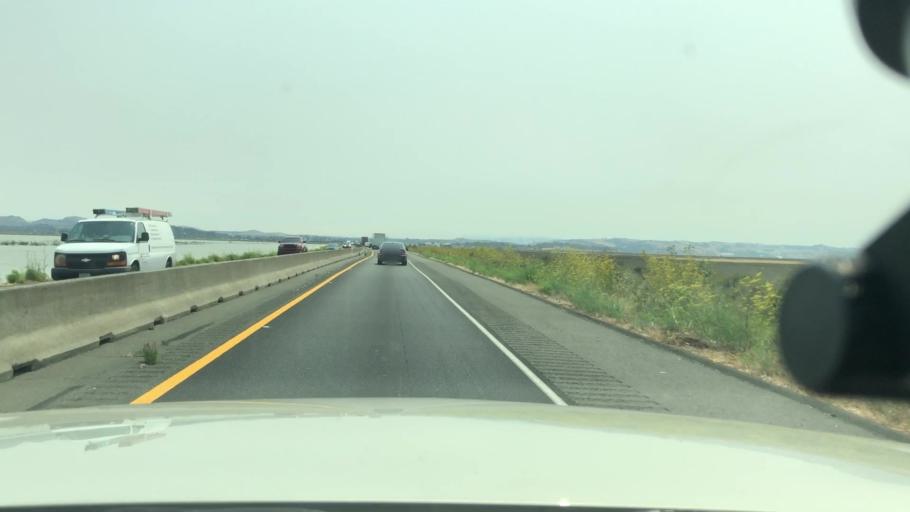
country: US
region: California
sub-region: Solano County
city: Vallejo
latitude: 38.1307
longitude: -122.3339
